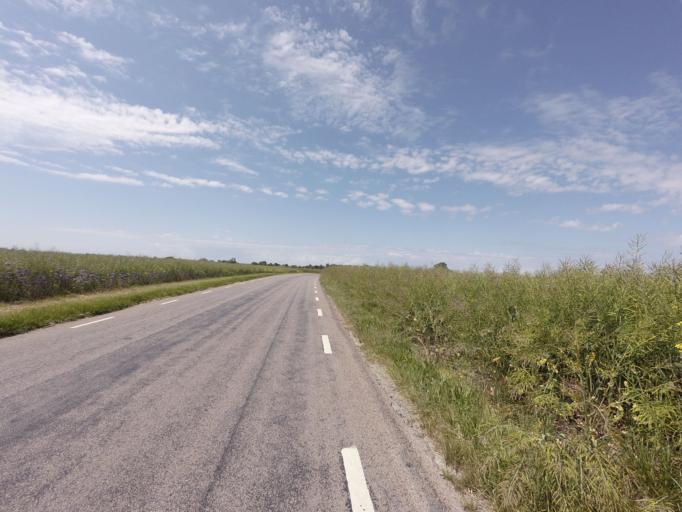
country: SE
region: Skane
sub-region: Trelleborgs Kommun
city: Skare
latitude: 55.4242
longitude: 13.0975
